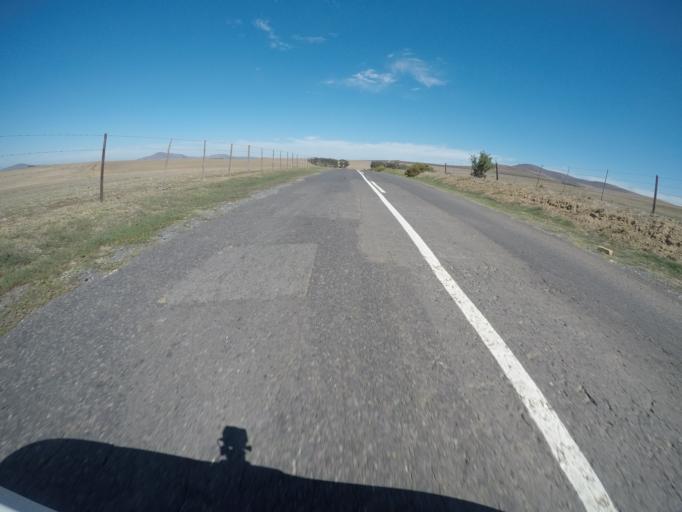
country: ZA
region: Western Cape
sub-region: City of Cape Town
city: Atlantis
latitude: -33.6933
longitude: 18.5930
